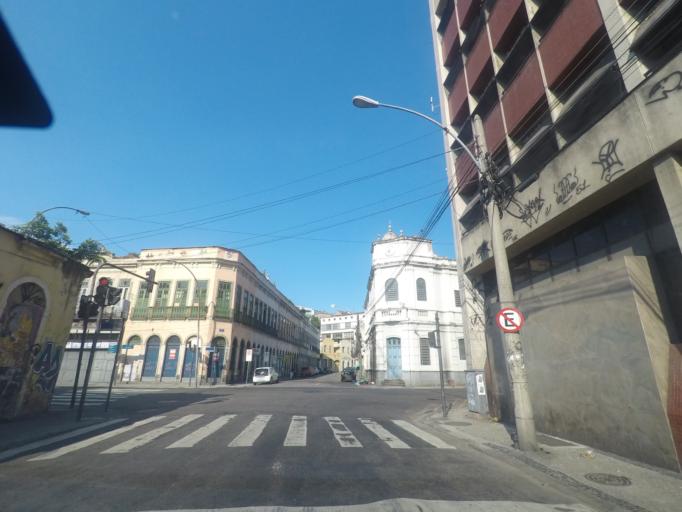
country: BR
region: Rio de Janeiro
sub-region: Rio De Janeiro
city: Rio de Janeiro
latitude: -22.9000
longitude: -43.1875
